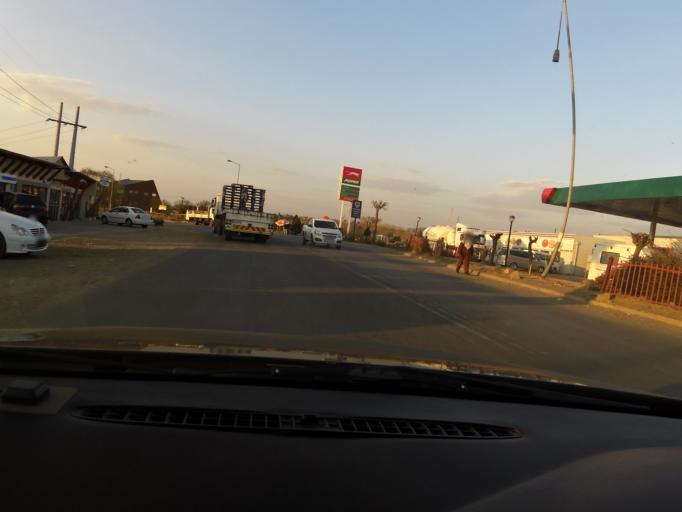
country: LS
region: Maseru
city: Maseru
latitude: -29.3151
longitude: 27.5104
